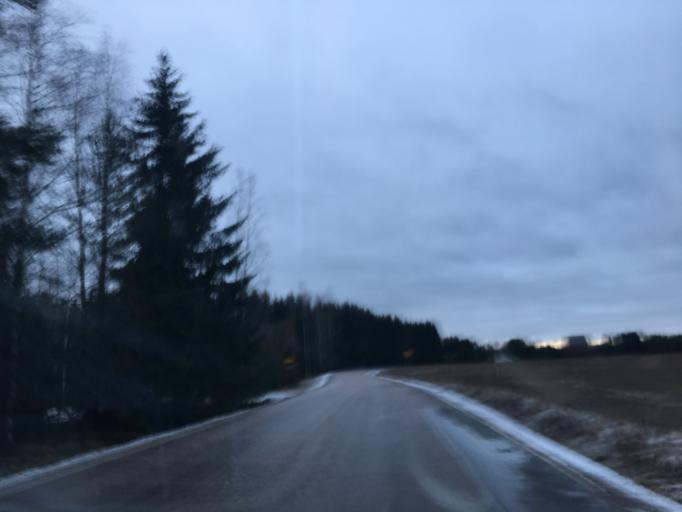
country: FI
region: Varsinais-Suomi
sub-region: Loimaa
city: Aura
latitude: 60.6328
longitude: 22.5884
